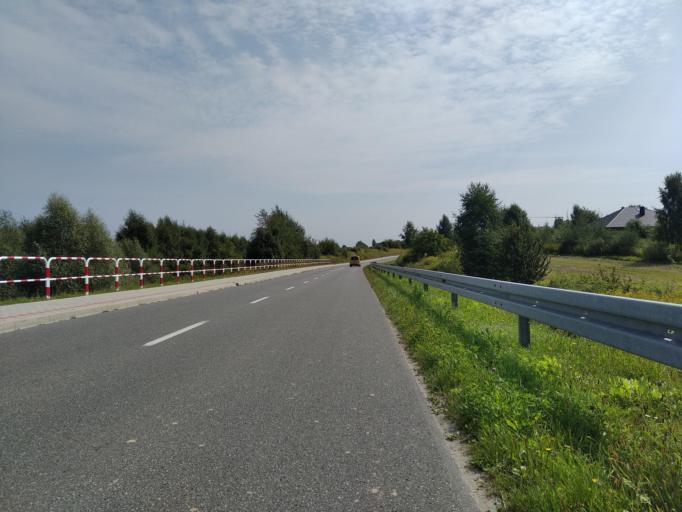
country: PL
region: Subcarpathian Voivodeship
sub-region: Powiat ropczycko-sedziszowski
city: Ropczyce
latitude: 50.0686
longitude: 21.5993
